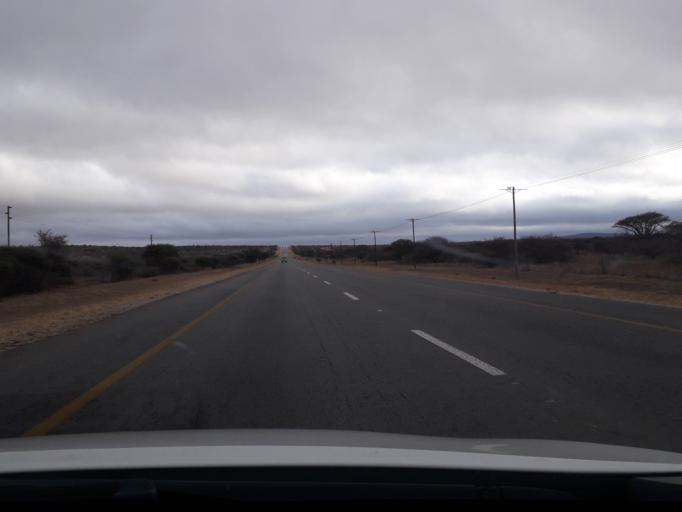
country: ZA
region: Limpopo
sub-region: Capricorn District Municipality
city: Polokwane
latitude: -23.6525
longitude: 29.6184
